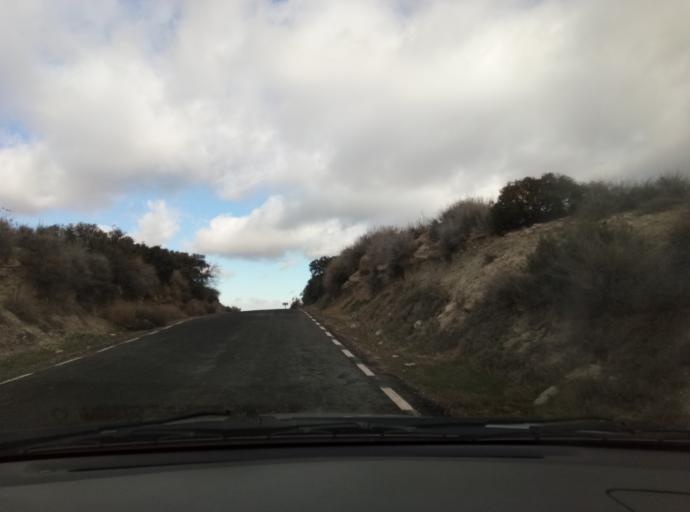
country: ES
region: Catalonia
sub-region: Provincia de Lleida
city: Nalec
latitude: 41.5886
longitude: 1.0851
